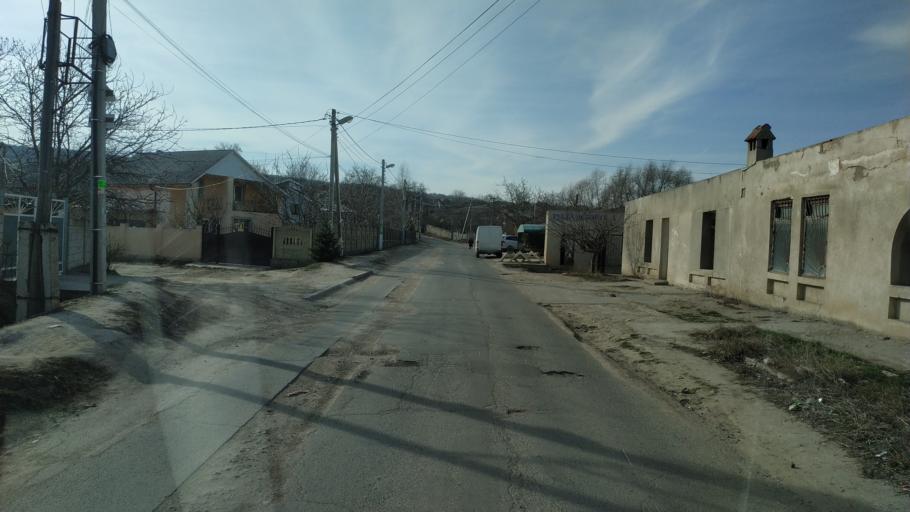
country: MD
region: Chisinau
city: Vatra
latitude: 47.0720
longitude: 28.6833
